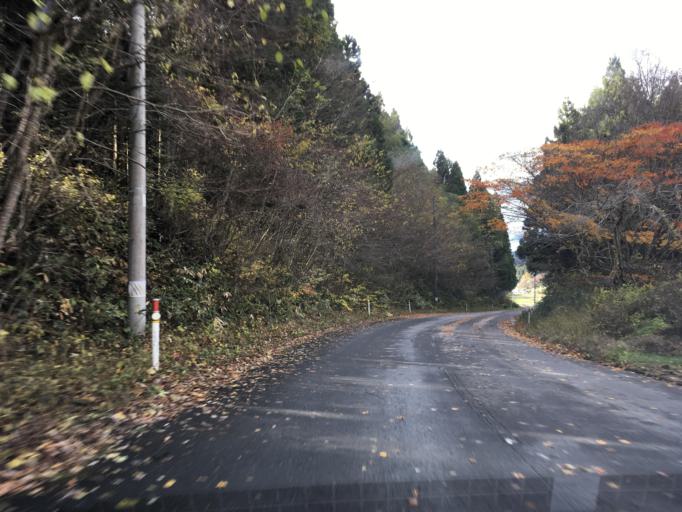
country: JP
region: Iwate
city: Ofunato
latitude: 38.8882
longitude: 141.4590
